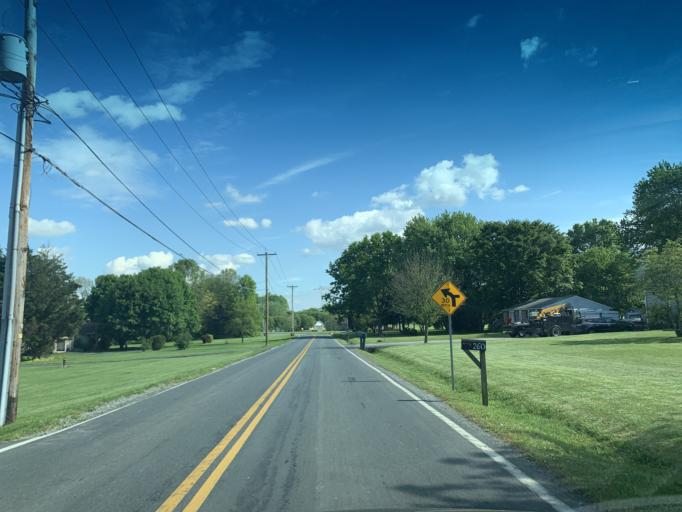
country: US
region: Maryland
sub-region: Cecil County
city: Rising Sun
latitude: 39.6956
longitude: -76.1406
